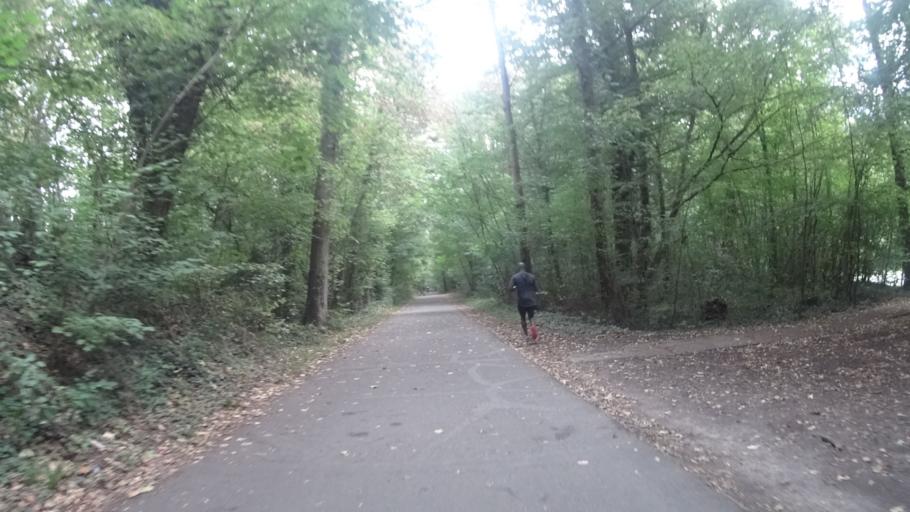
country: FR
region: Ile-de-France
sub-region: Departement de Seine-Saint-Denis
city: Livry-Gargan
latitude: 48.9380
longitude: 2.5486
